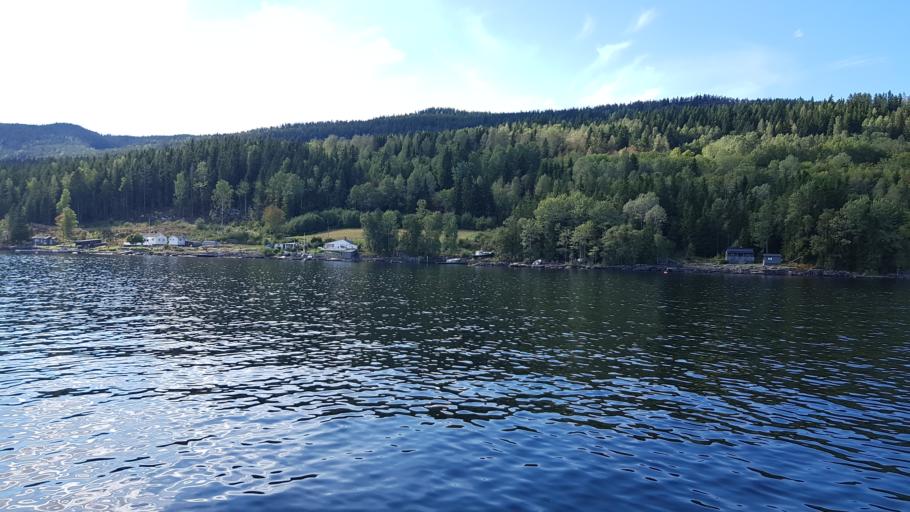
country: NO
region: Akershus
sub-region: Hurdal
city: Hurdal
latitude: 60.5452
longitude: 11.1984
